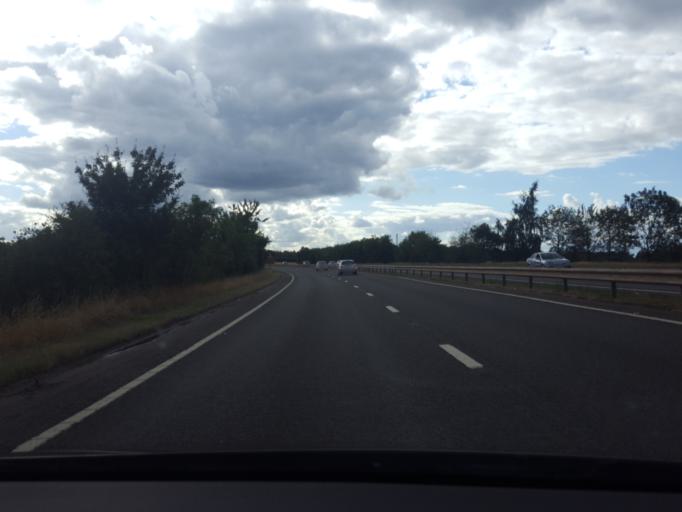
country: GB
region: England
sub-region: Leicestershire
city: Quorndon
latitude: 52.7523
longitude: -1.1756
